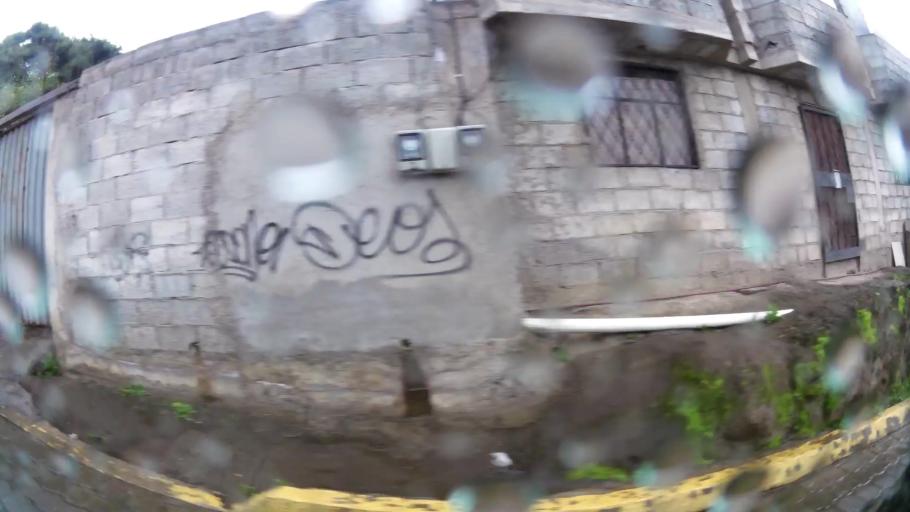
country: EC
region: Pichincha
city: Quito
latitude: -0.0982
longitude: -78.5110
